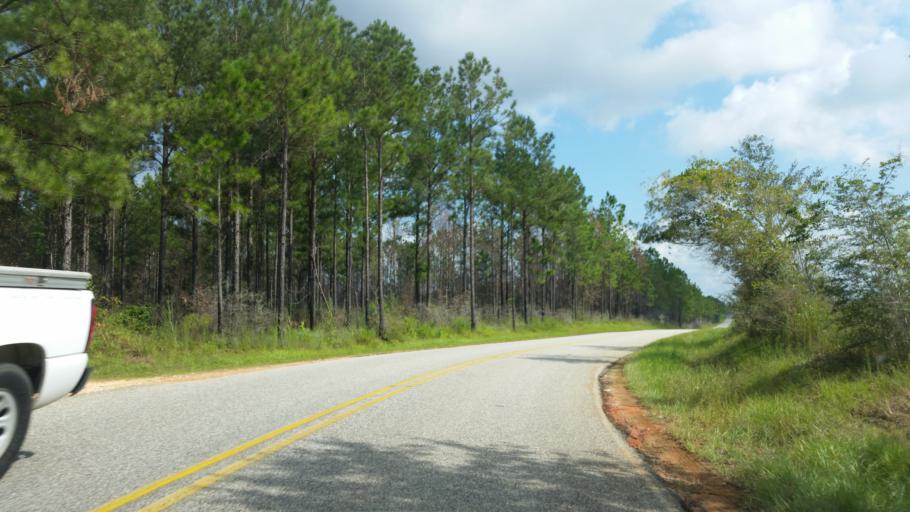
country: US
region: Florida
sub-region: Escambia County
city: Cantonment
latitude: 30.6797
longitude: -87.4705
